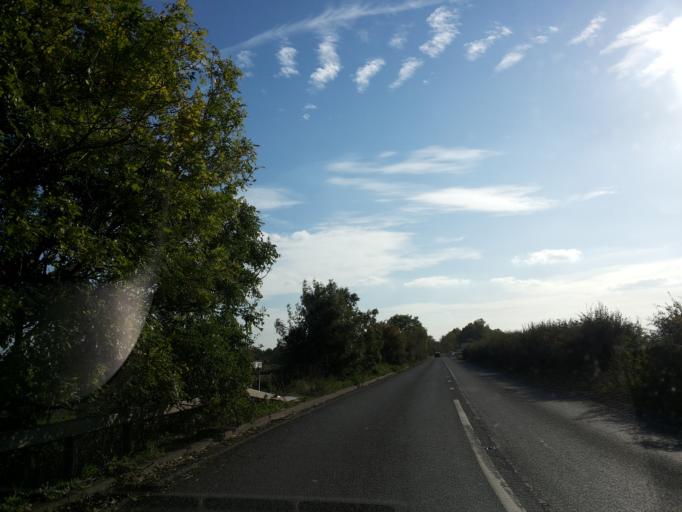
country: GB
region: England
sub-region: East Riding of Yorkshire
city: Rawcliffe
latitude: 53.6853
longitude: -0.9854
